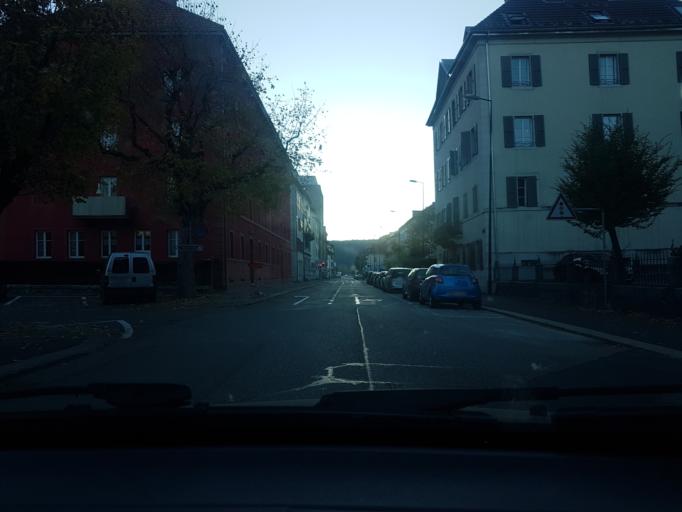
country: CH
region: Neuchatel
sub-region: Le Locle District
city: Le Locle
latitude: 47.0563
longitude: 6.7457
